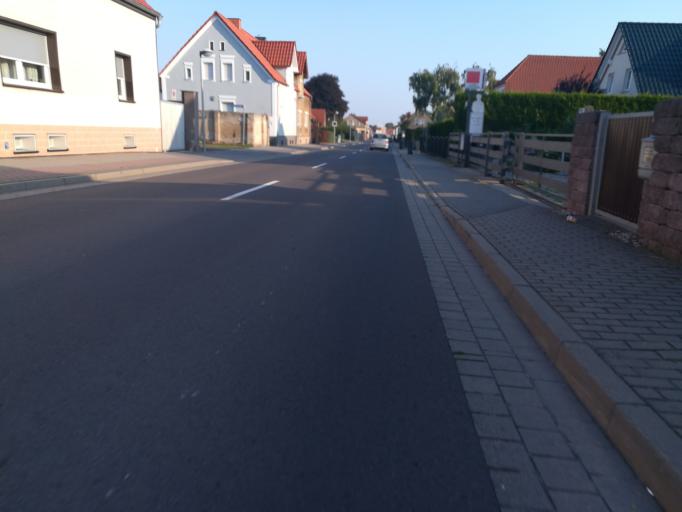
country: DE
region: Saxony-Anhalt
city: Irxleben
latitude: 52.1622
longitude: 11.4847
